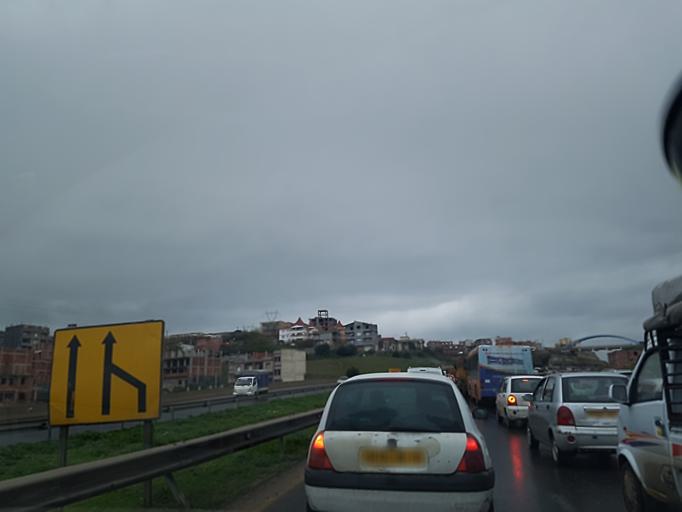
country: DZ
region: Boumerdes
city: Ouled Moussa
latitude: 36.6785
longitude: 3.3803
